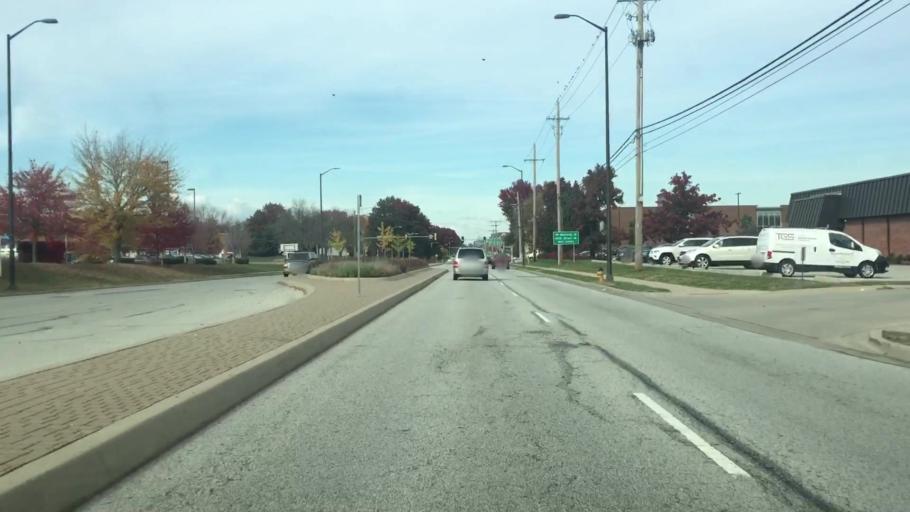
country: US
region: Kansas
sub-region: Johnson County
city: Lenexa
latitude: 38.9729
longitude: -94.7236
